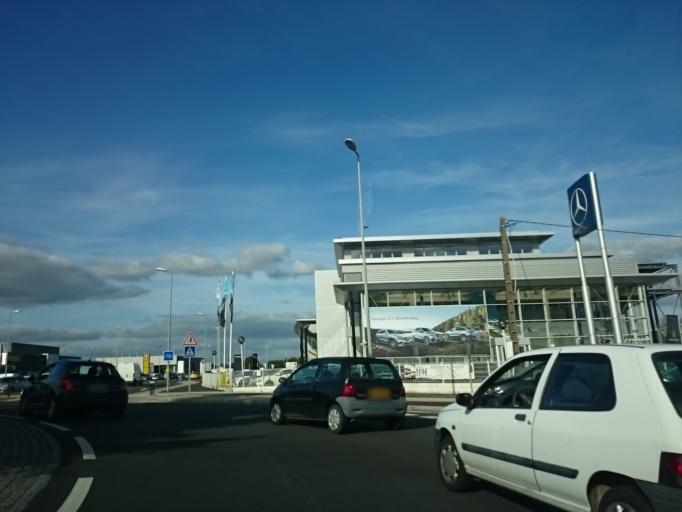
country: FR
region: Pays de la Loire
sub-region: Departement de la Loire-Atlantique
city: Orvault
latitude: 47.2543
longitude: -1.6290
